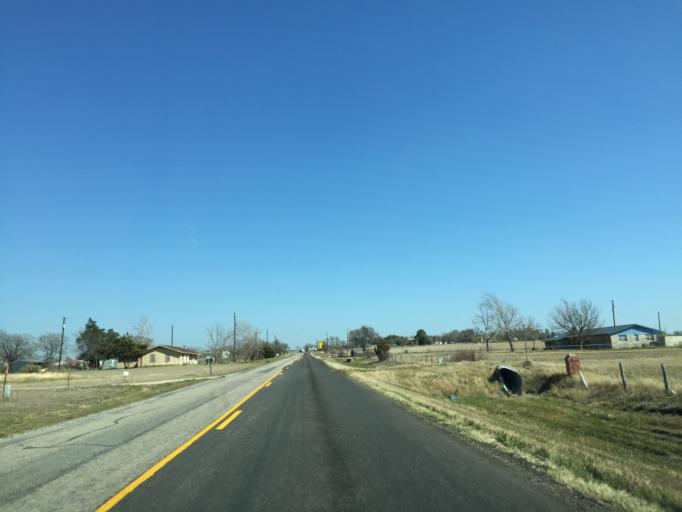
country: US
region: Texas
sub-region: Williamson County
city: Serenada
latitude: 30.7077
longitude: -97.5821
